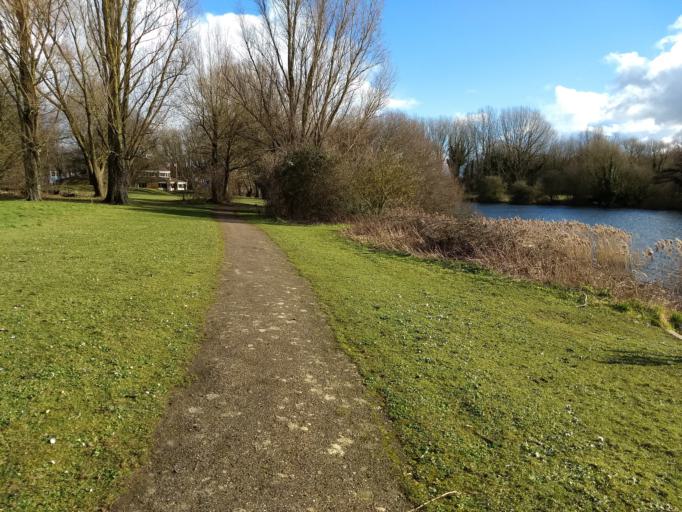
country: GB
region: England
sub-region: Buckinghamshire
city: Bletchley
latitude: 52.0077
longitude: -0.7232
